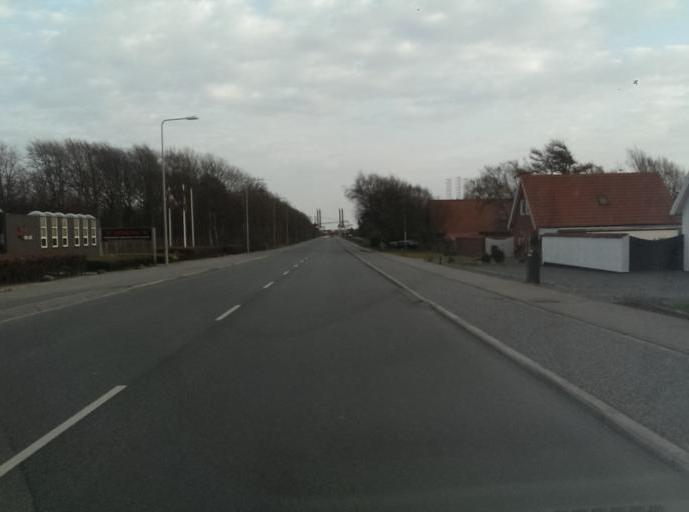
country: DK
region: South Denmark
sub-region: Esbjerg Kommune
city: Esbjerg
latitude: 55.4930
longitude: 8.4104
